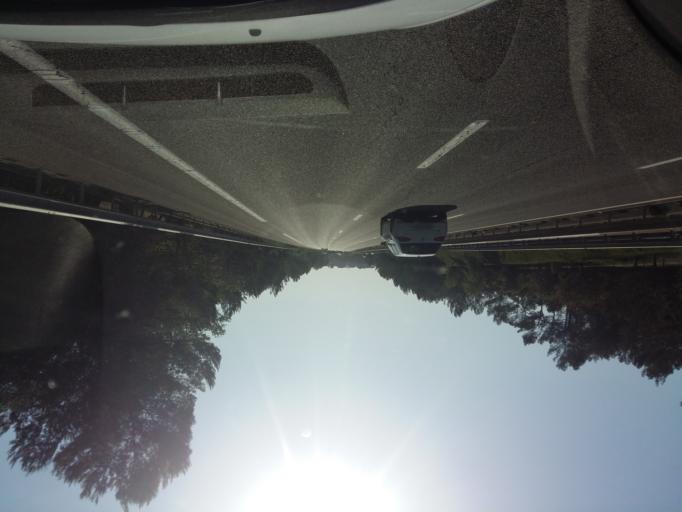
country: FR
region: Provence-Alpes-Cote d'Azur
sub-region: Departement du Var
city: Bras
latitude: 43.4251
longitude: 5.9734
